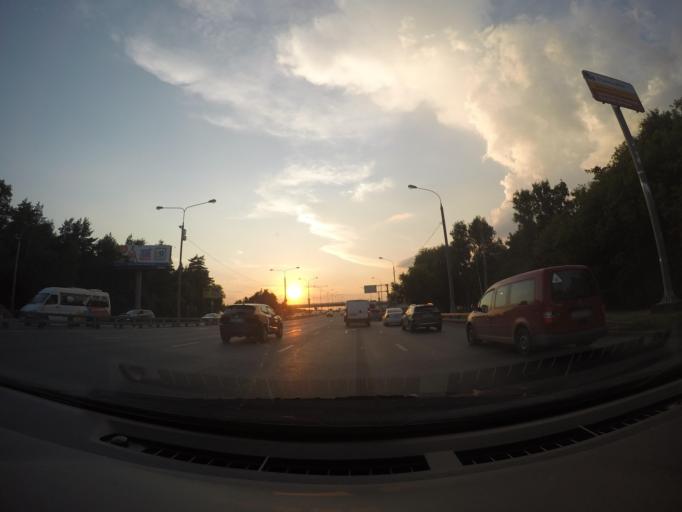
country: RU
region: Moscow
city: Zhulebino
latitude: 55.6845
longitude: 37.8376
